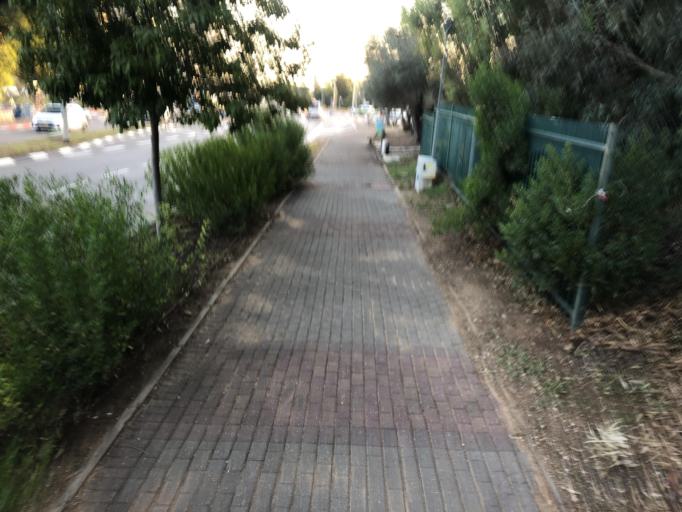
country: IL
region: Northern District
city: `Akko
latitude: 32.9228
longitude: 35.0917
